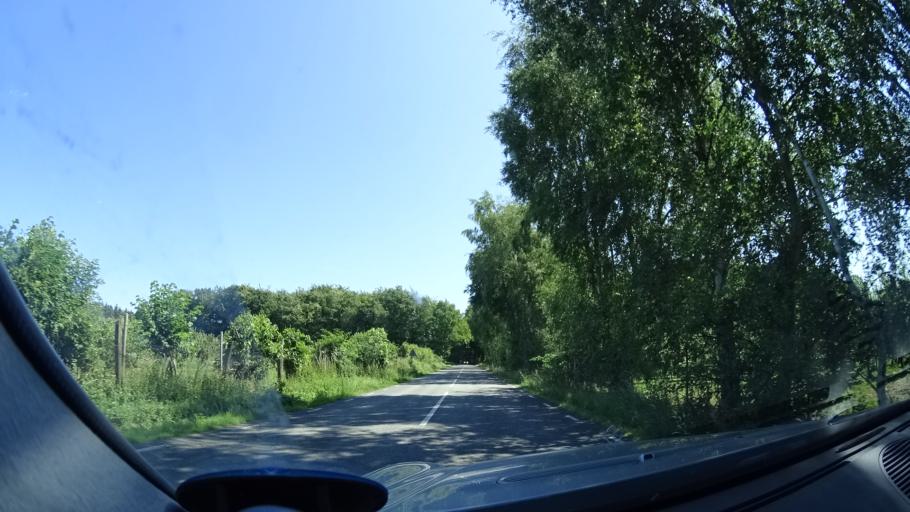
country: SE
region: Skane
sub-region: Kristianstads Kommun
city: Degeberga
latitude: 55.8909
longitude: 14.0072
